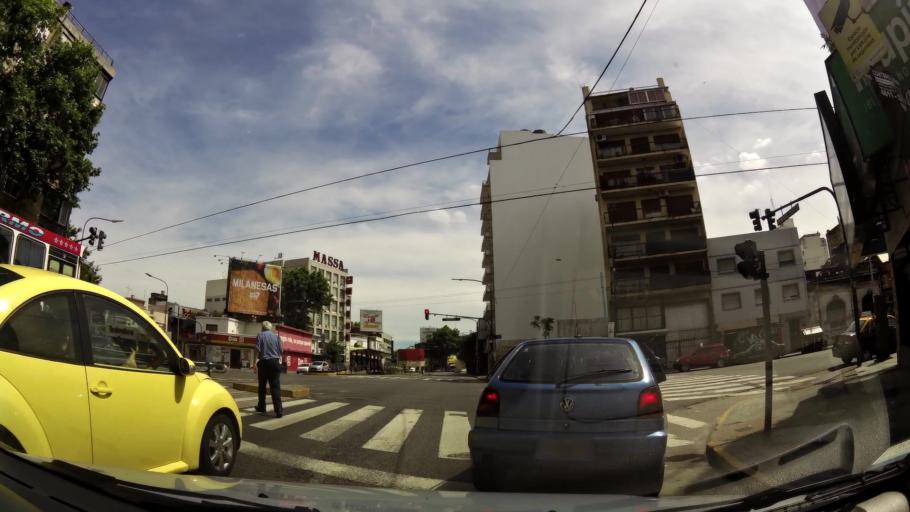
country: AR
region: Buenos Aires F.D.
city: Villa Santa Rita
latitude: -34.6179
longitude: -58.4760
